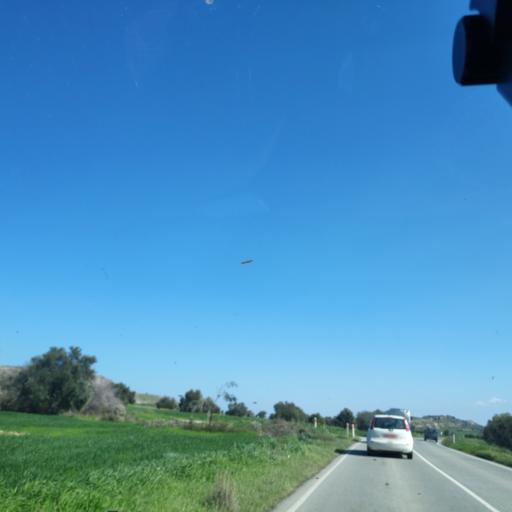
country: CY
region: Lefkosia
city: Tseri
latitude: 35.0142
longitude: 33.3389
